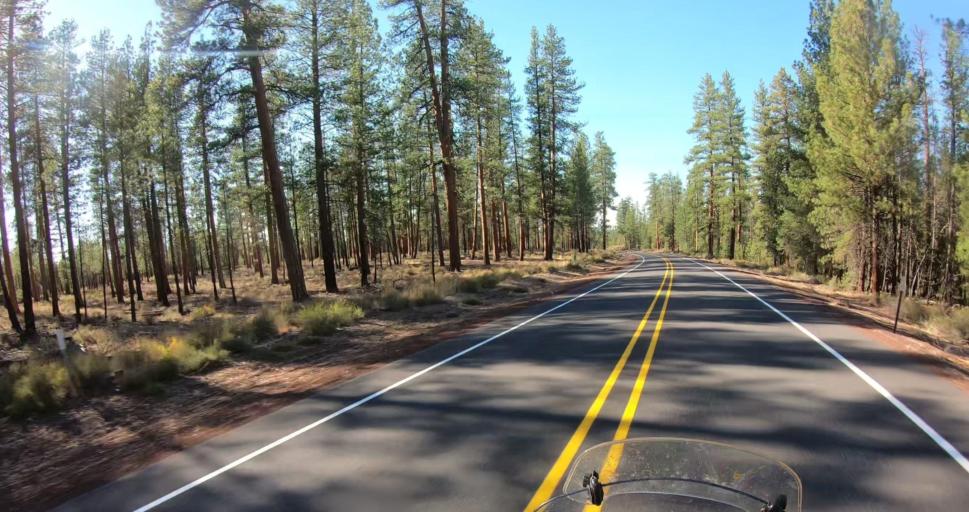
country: US
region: Oregon
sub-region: Deschutes County
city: La Pine
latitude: 43.4718
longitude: -121.4010
